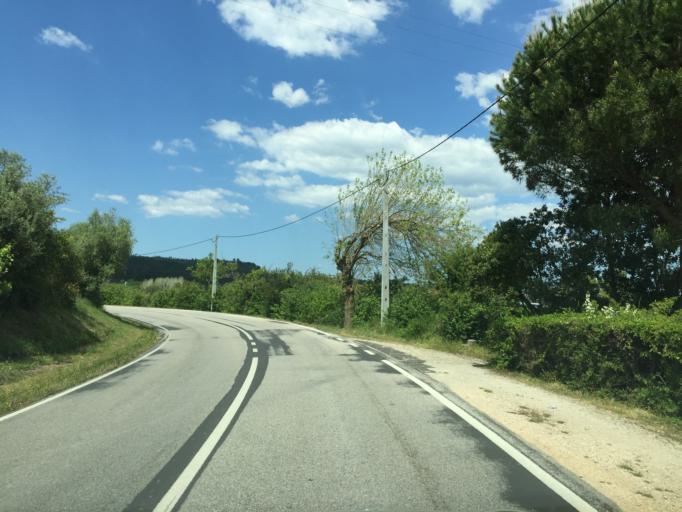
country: PT
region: Santarem
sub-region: Ourem
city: Ourem
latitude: 39.6452
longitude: -8.6108
